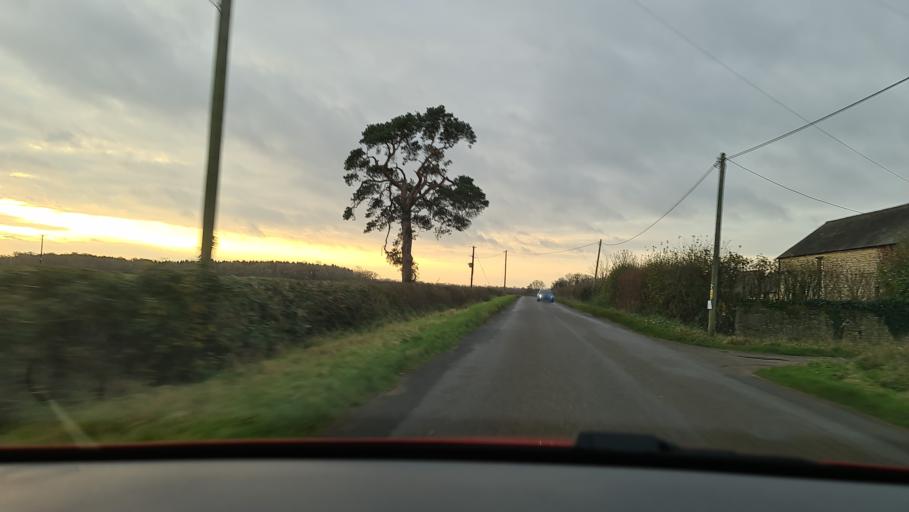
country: GB
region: England
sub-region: Oxfordshire
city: Somerton
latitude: 51.9085
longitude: -1.2753
